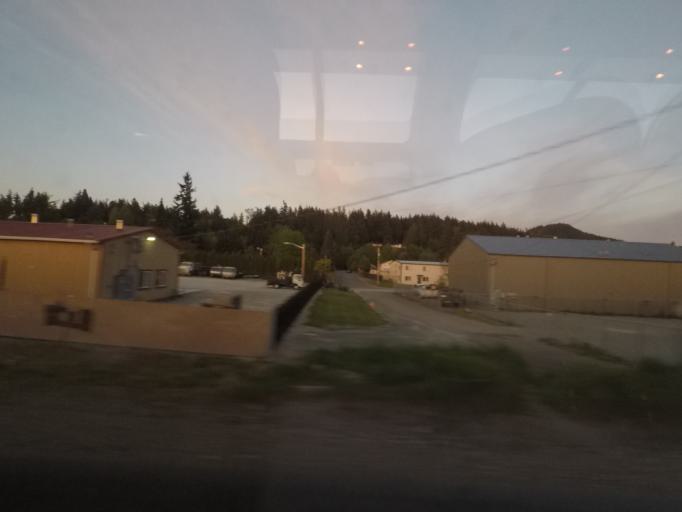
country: US
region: Washington
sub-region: Skagit County
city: Mount Vernon
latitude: 48.4094
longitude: -122.3357
